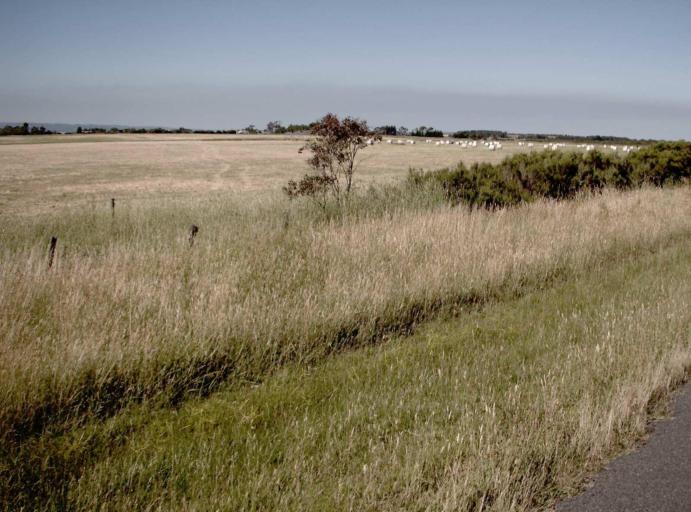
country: AU
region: Victoria
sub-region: Latrobe
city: Traralgon
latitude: -38.6347
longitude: 146.5837
